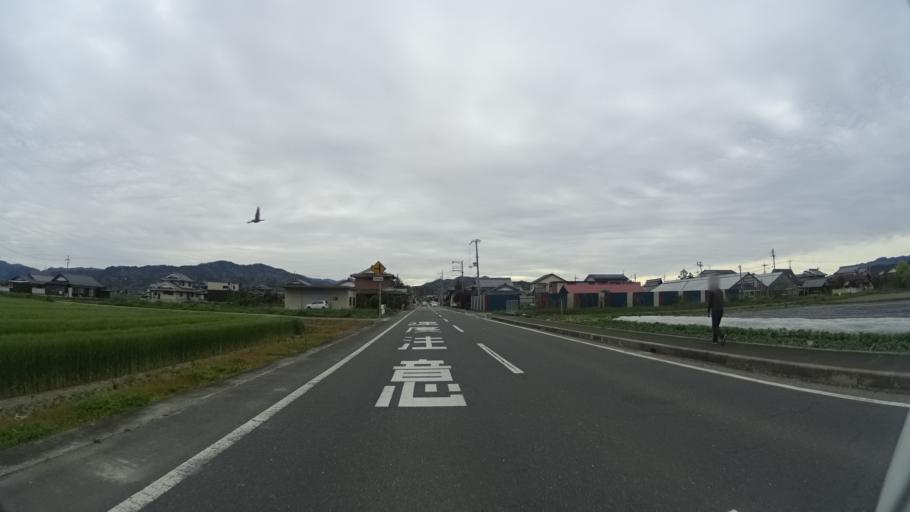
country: JP
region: Kyoto
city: Kameoka
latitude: 35.0543
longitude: 135.5673
